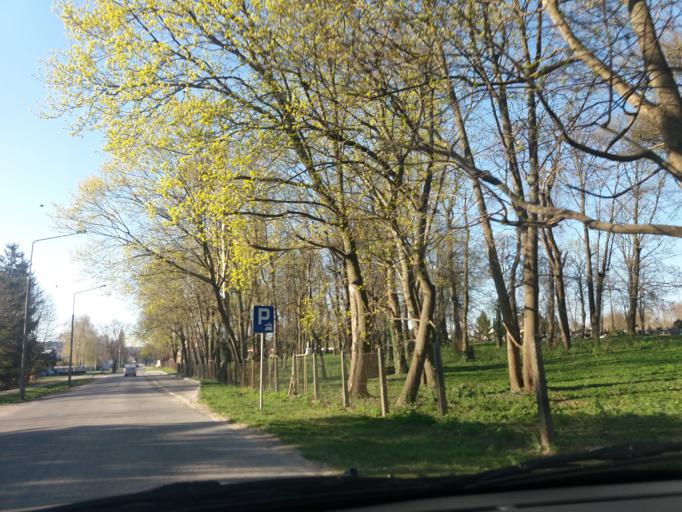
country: PL
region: Warmian-Masurian Voivodeship
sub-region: Powiat nidzicki
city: Nidzica
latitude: 53.3512
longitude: 20.4290
